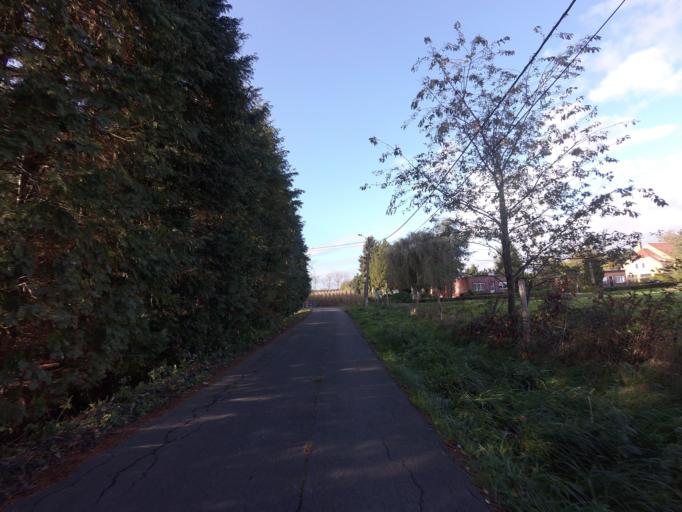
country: BE
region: Flanders
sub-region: Provincie Antwerpen
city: Bonheiden
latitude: 51.0280
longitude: 4.5777
